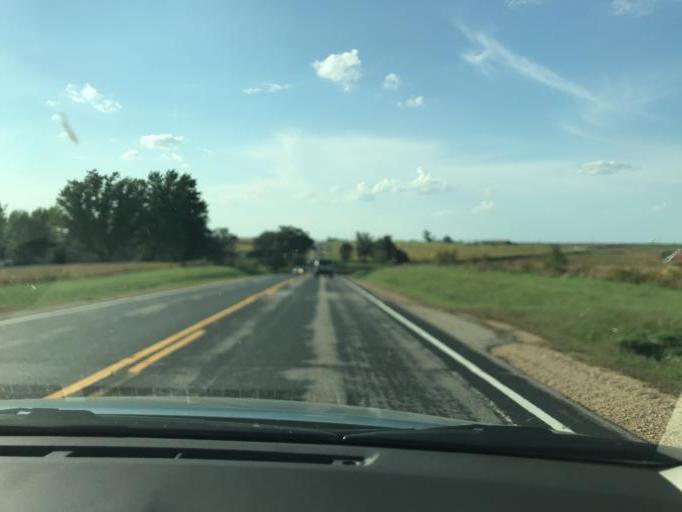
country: US
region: Wisconsin
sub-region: Grant County
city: Platteville
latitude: 42.7052
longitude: -90.4432
